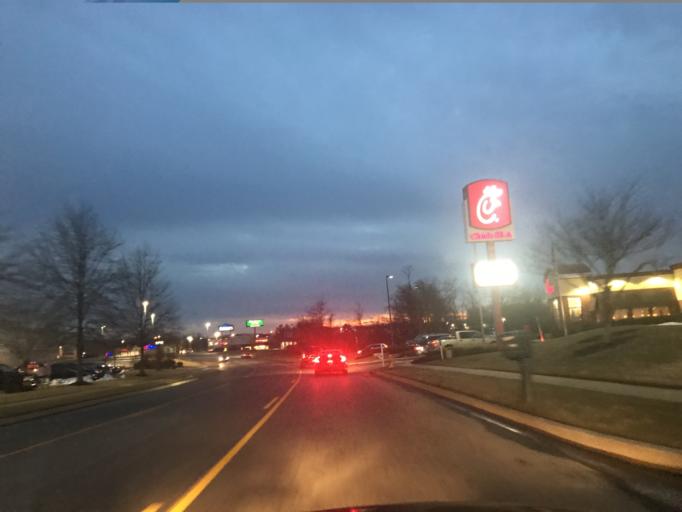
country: US
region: Maryland
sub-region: Harford County
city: Joppatowne
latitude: 39.4613
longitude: -76.3177
